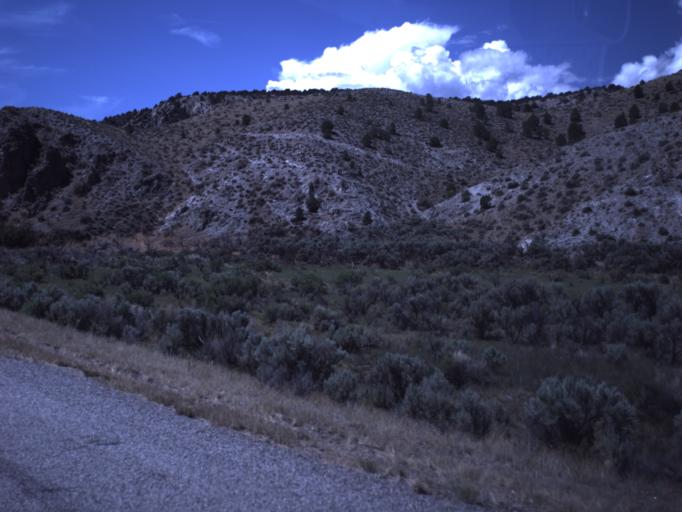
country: US
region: Utah
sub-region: Piute County
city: Junction
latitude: 38.0479
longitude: -112.3536
